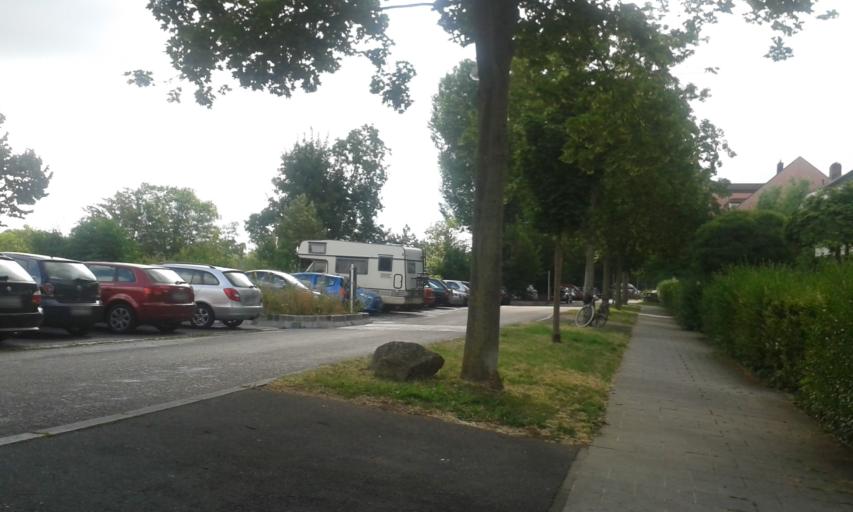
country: DE
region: Bavaria
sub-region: Upper Franconia
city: Bamberg
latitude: 49.9003
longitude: 10.8802
